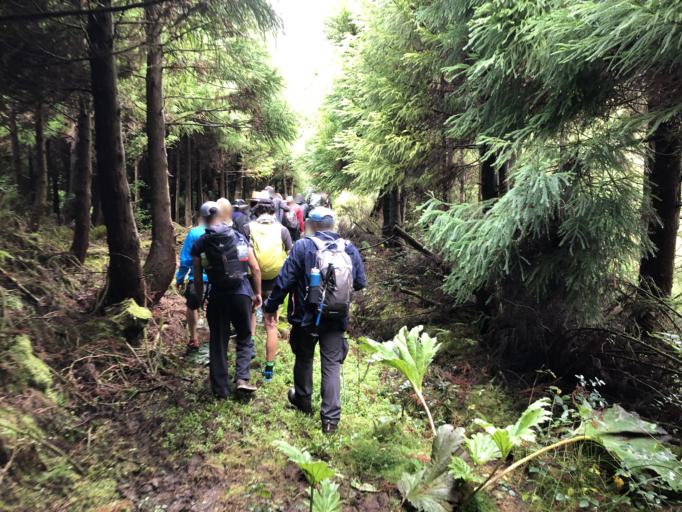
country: PT
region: Azores
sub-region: Ponta Delgada
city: Arrifes
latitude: 37.8322
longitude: -25.7590
